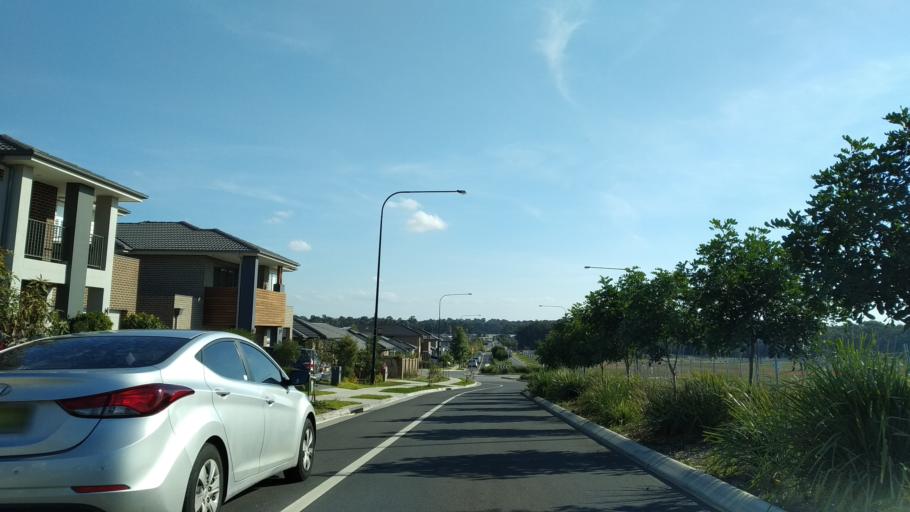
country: AU
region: New South Wales
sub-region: Blacktown
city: Hassall Grove
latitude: -33.7226
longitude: 150.8528
